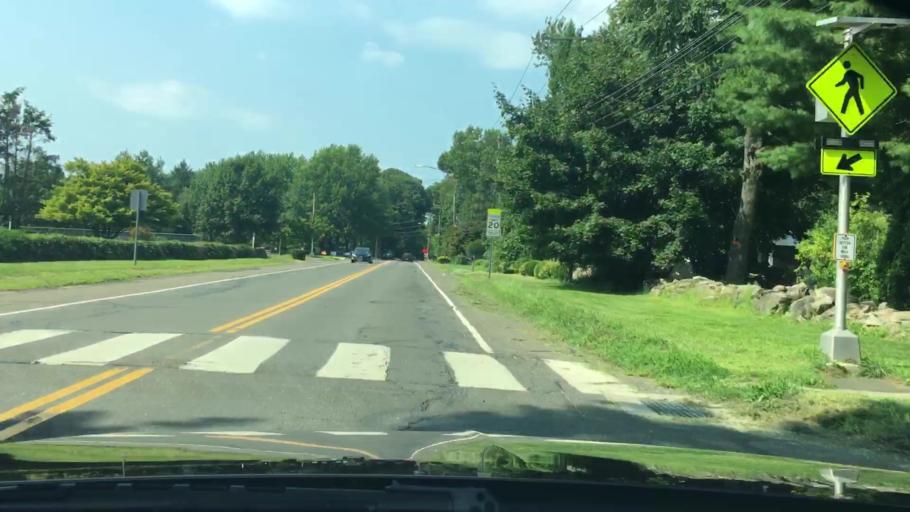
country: US
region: Connecticut
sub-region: Fairfield County
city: Norwalk
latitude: 41.1363
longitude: -73.4149
